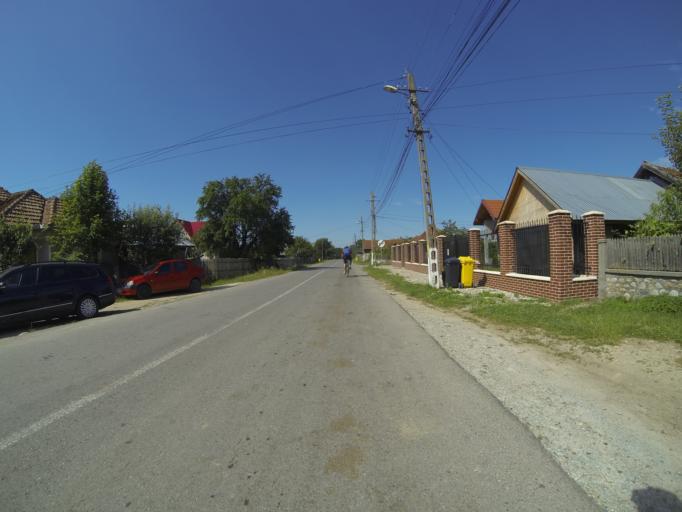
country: RO
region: Gorj
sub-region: Comuna Polovragi
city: Polovragi
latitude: 45.1664
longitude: 23.8135
